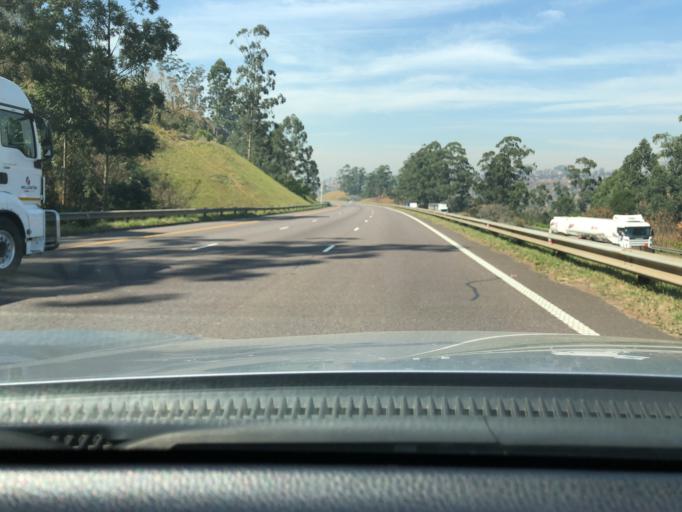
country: ZA
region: KwaZulu-Natal
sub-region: eThekwini Metropolitan Municipality
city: Mpumalanga
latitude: -29.8207
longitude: 30.7778
